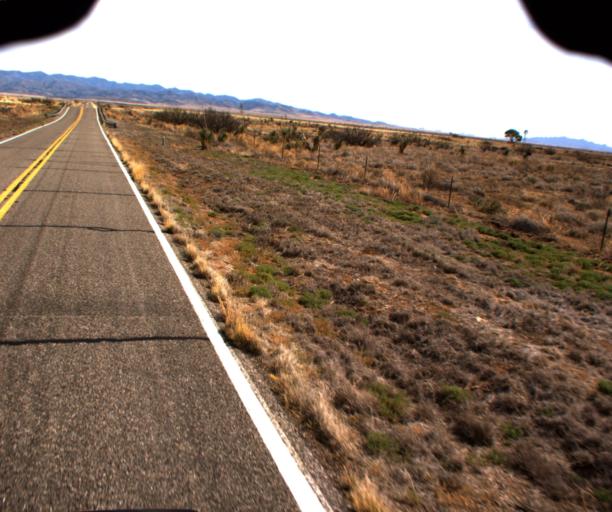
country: US
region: Arizona
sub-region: Cochise County
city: Willcox
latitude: 32.0779
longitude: -109.5187
